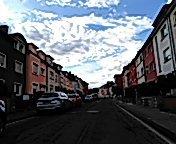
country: LU
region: Luxembourg
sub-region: Canton d'Esch-sur-Alzette
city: Esch-sur-Alzette
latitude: 49.5010
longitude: 5.9737
